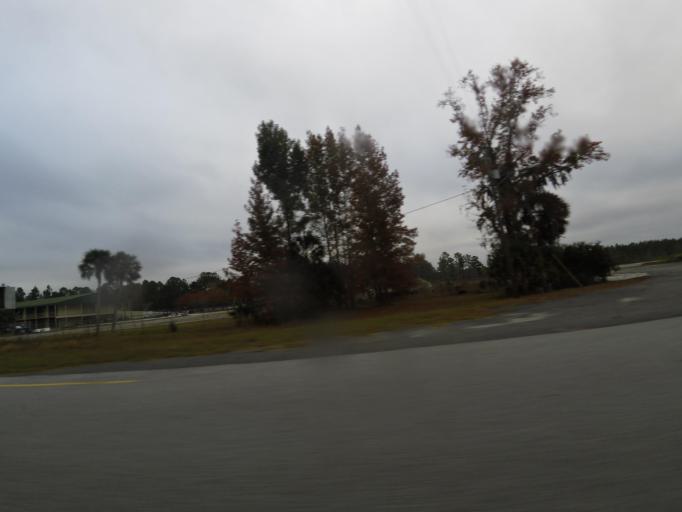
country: US
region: Georgia
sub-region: Charlton County
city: Folkston
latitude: 30.8643
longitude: -82.0132
